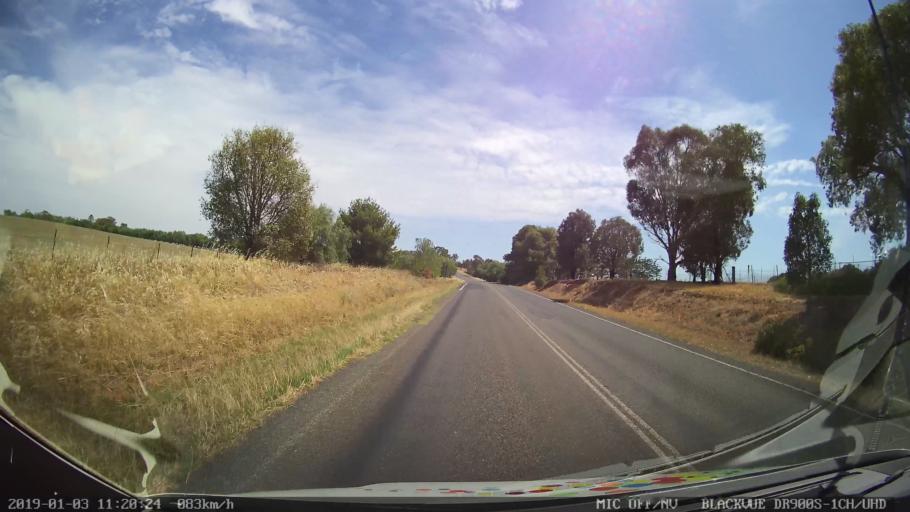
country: AU
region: New South Wales
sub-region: Young
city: Young
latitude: -34.1016
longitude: 148.2549
